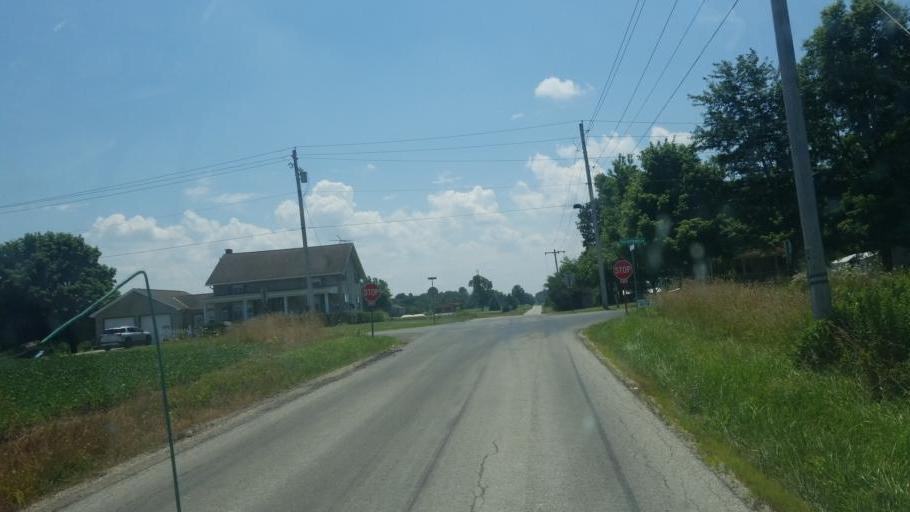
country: US
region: Ohio
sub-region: Richland County
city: Ontario
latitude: 40.8582
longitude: -82.5520
